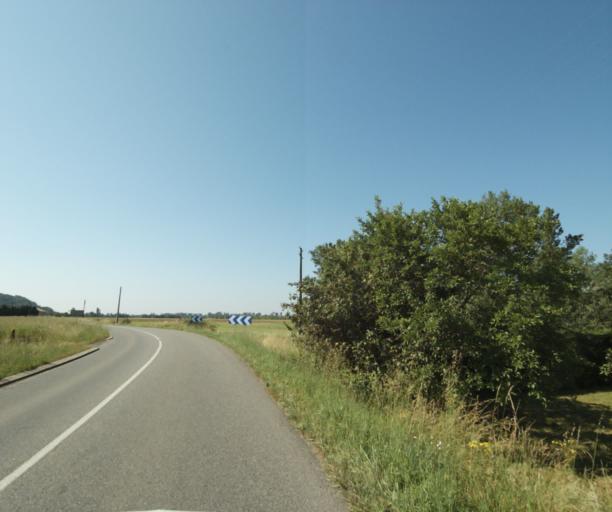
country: FR
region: Midi-Pyrenees
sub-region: Departement du Tarn-et-Garonne
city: Bressols
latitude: 43.9655
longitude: 1.3582
